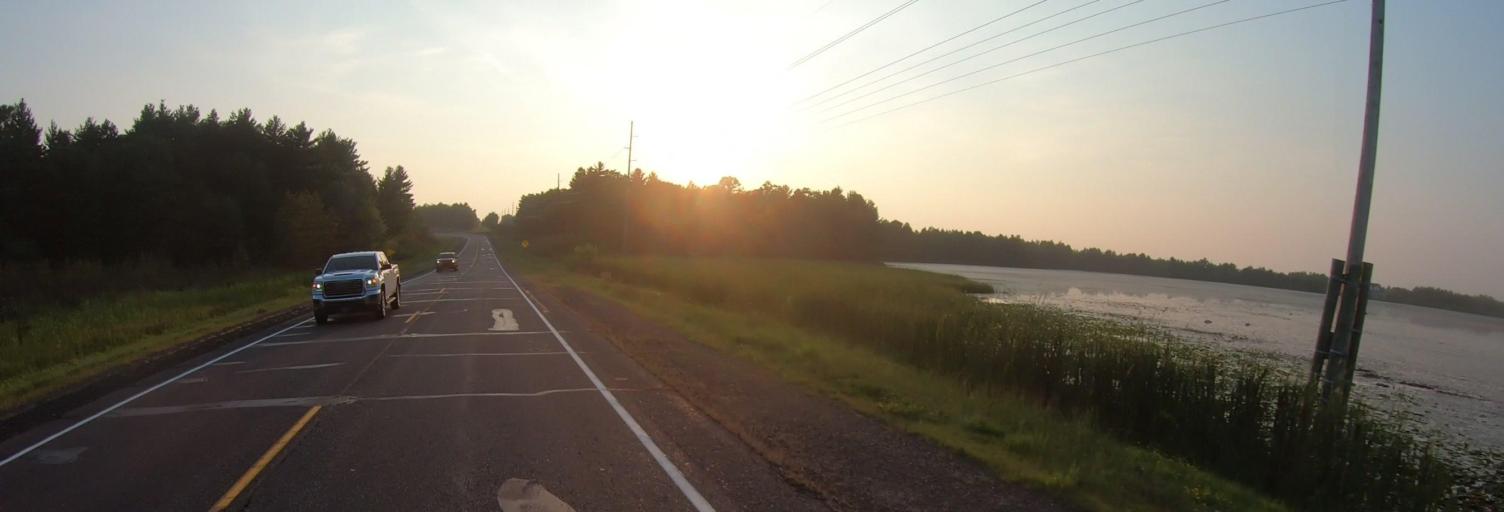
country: US
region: Wisconsin
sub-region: Burnett County
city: Siren
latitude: 45.7844
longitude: -92.4154
